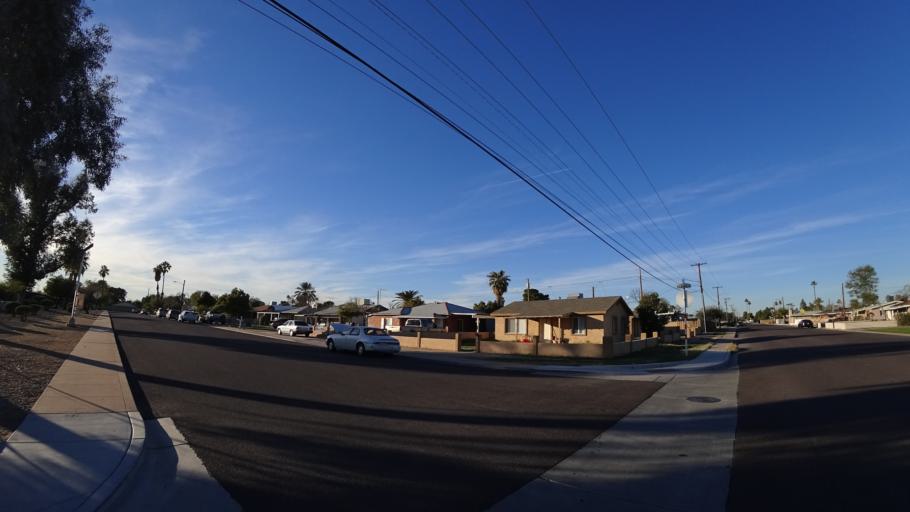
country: US
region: Arizona
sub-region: Maricopa County
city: Phoenix
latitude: 33.4749
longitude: -112.1044
